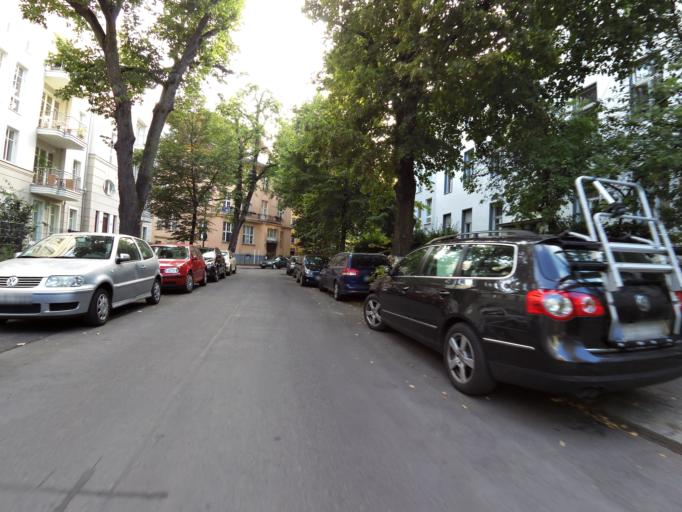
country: DE
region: Berlin
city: Friedenau
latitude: 52.4670
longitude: 13.3326
